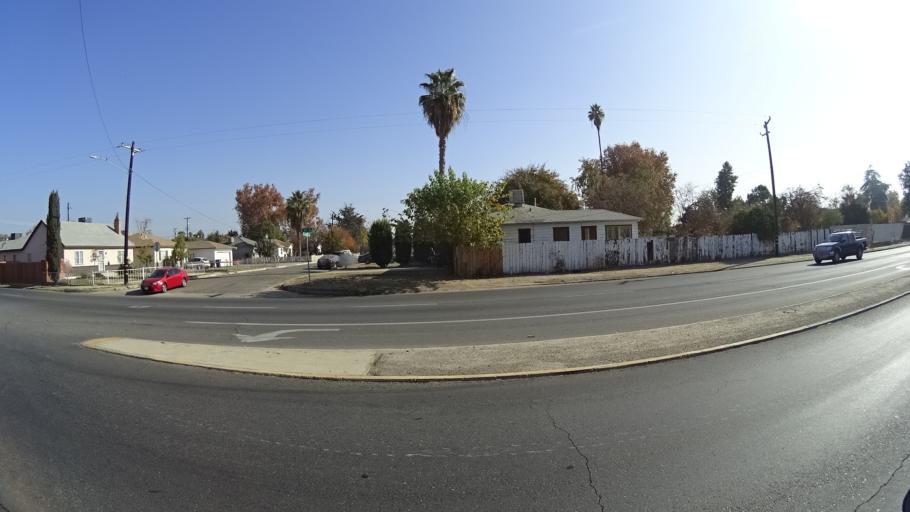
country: US
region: California
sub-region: Kern County
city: Bakersfield
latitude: 35.3493
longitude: -119.0213
